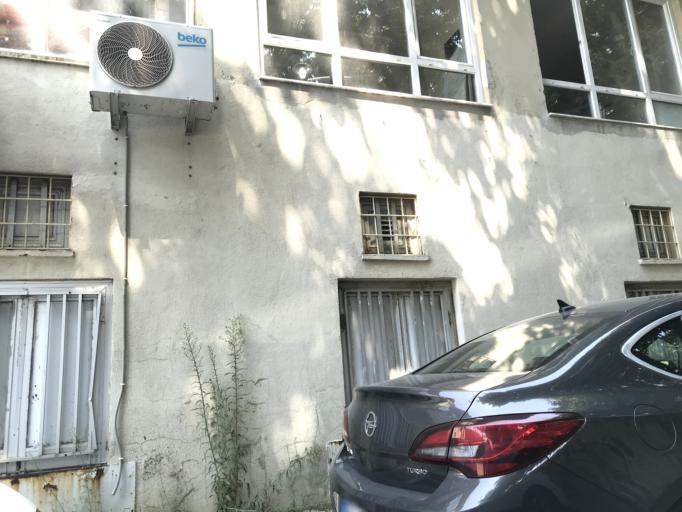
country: TR
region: Izmir
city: Selcuk
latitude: 37.9474
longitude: 27.3702
